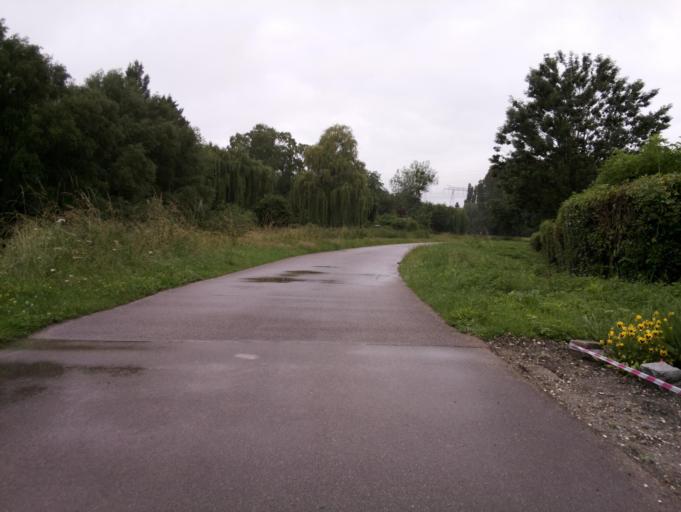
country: FR
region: Picardie
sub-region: Departement de la Somme
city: Dreuil-les-Amiens
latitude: 49.9204
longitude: 2.2165
